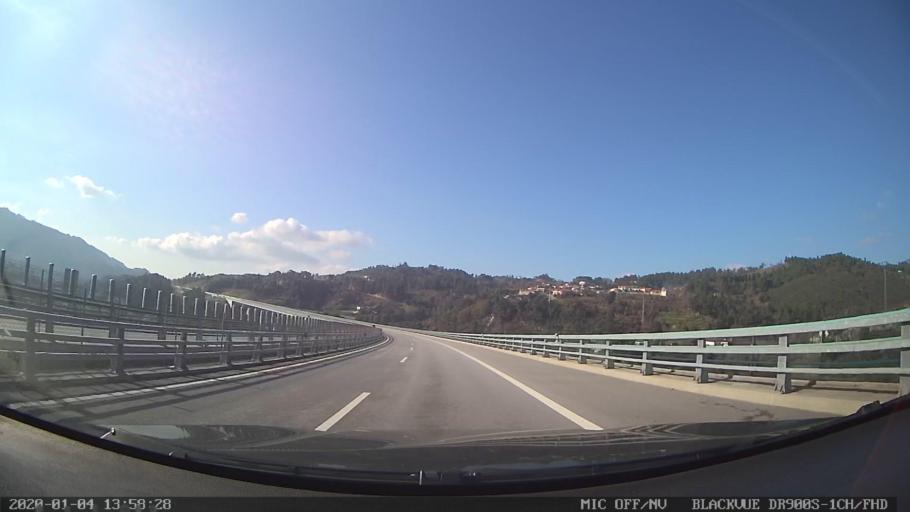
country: PT
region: Porto
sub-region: Amarante
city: Amarante
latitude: 41.2625
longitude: -8.0220
